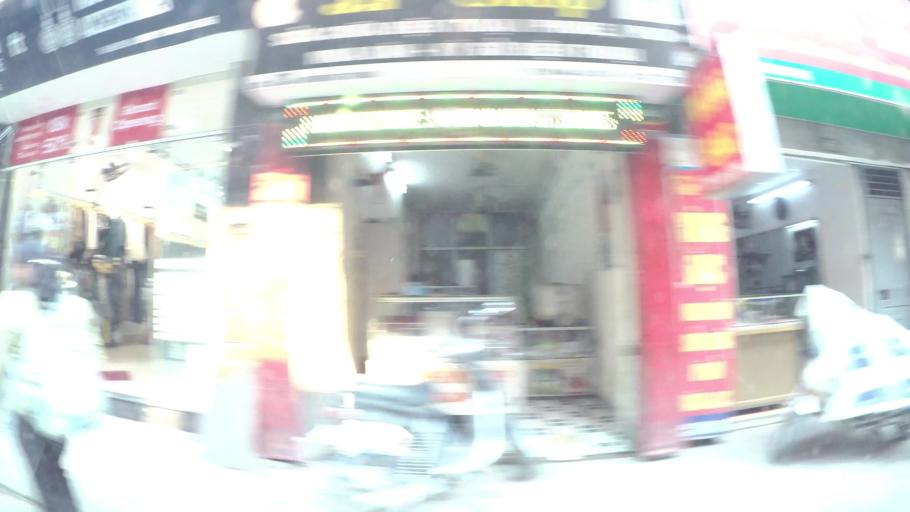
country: VN
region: Ha Noi
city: Thanh Xuan
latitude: 20.9988
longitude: 105.8186
